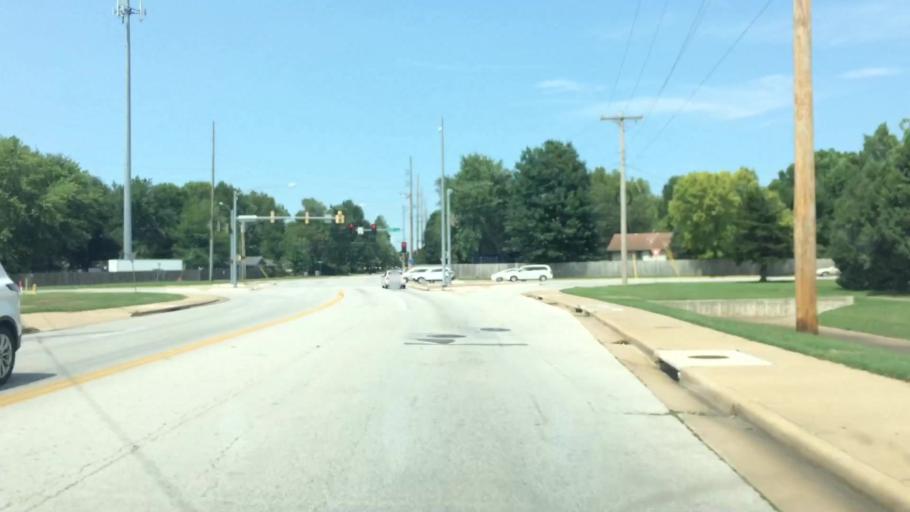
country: US
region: Missouri
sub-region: Greene County
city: Springfield
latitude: 37.1664
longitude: -93.2716
